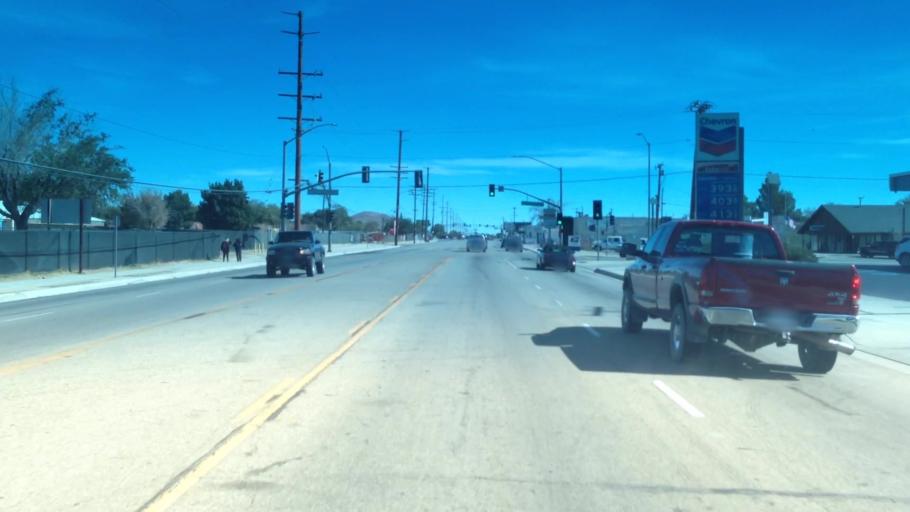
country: US
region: California
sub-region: Kern County
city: Rosamond
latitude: 34.8643
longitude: -118.1681
